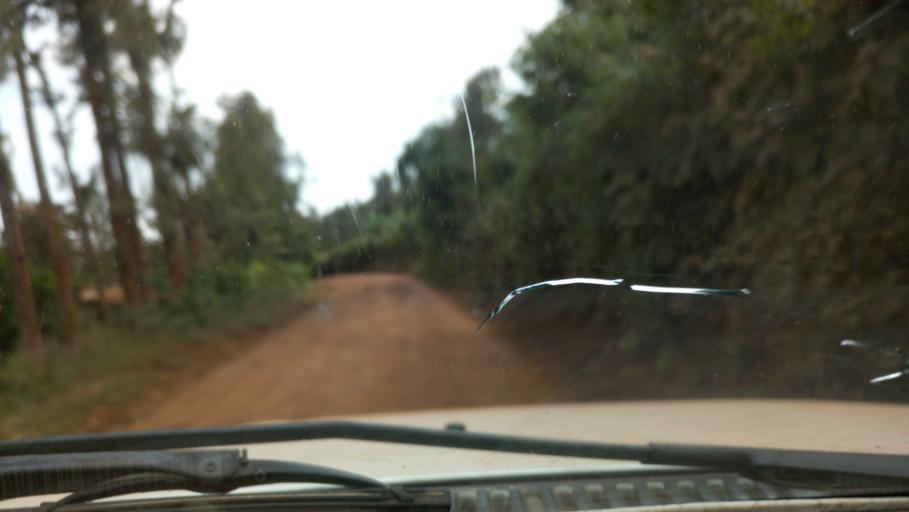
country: KE
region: Murang'a District
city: Maragua
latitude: -0.7831
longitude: 37.0913
